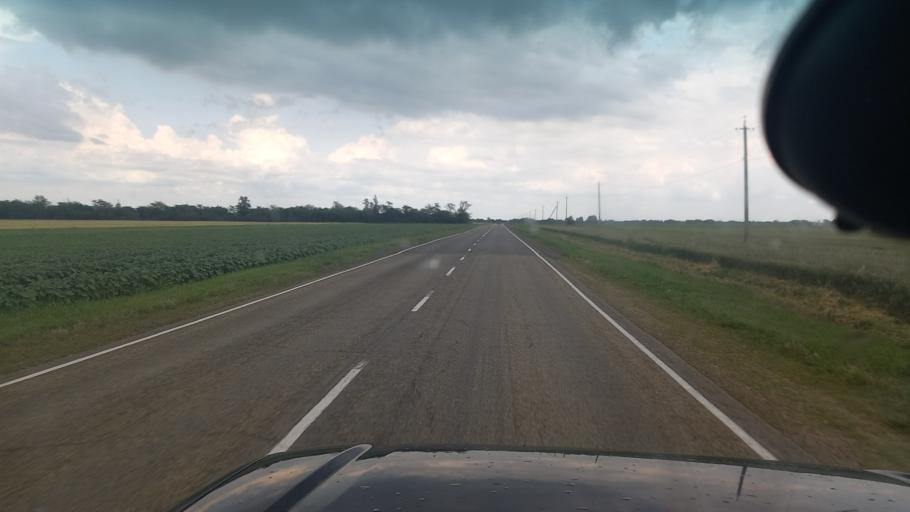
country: RU
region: Adygeya
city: Shovgenovskiy
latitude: 44.9953
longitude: 40.1194
